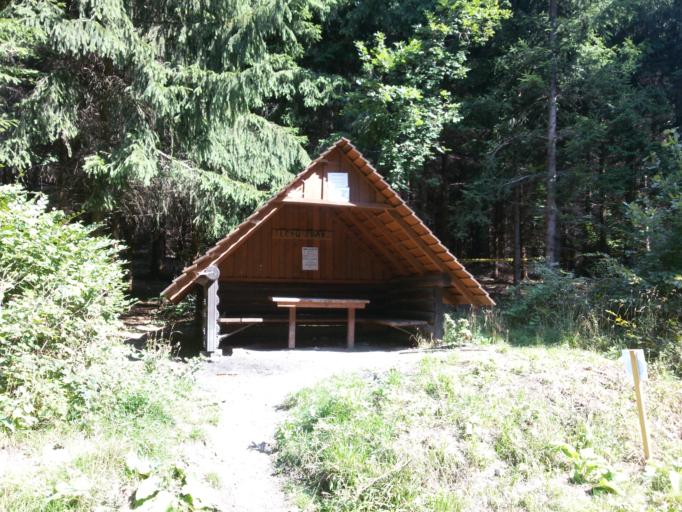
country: CZ
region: Zlin
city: Breznice
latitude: 49.1978
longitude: 17.6310
